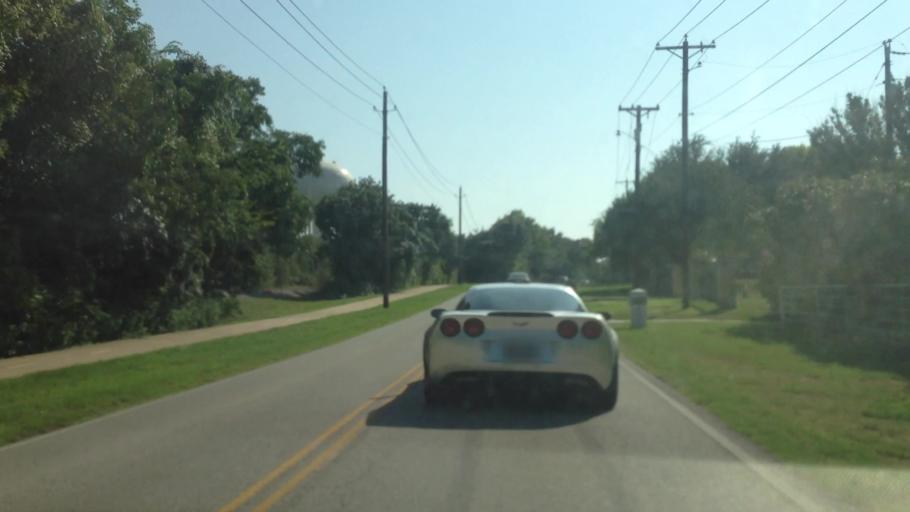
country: US
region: Texas
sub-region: Tarrant County
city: Colleyville
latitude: 32.8997
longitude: -97.1599
